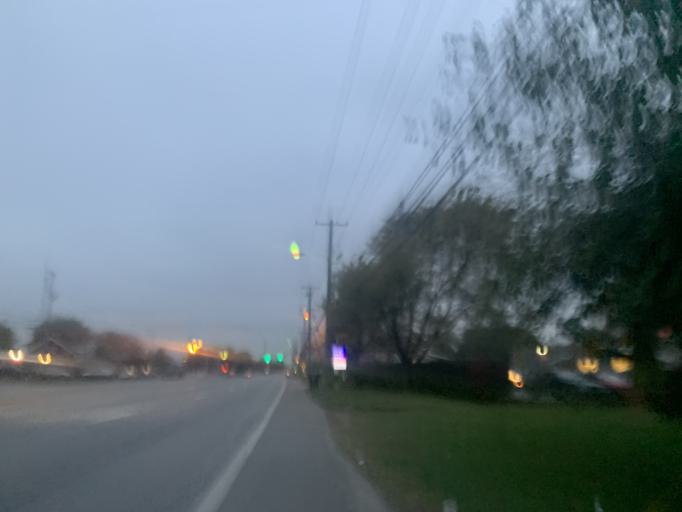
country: US
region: Kentucky
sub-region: Jefferson County
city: Shively
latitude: 38.2153
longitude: -85.7956
